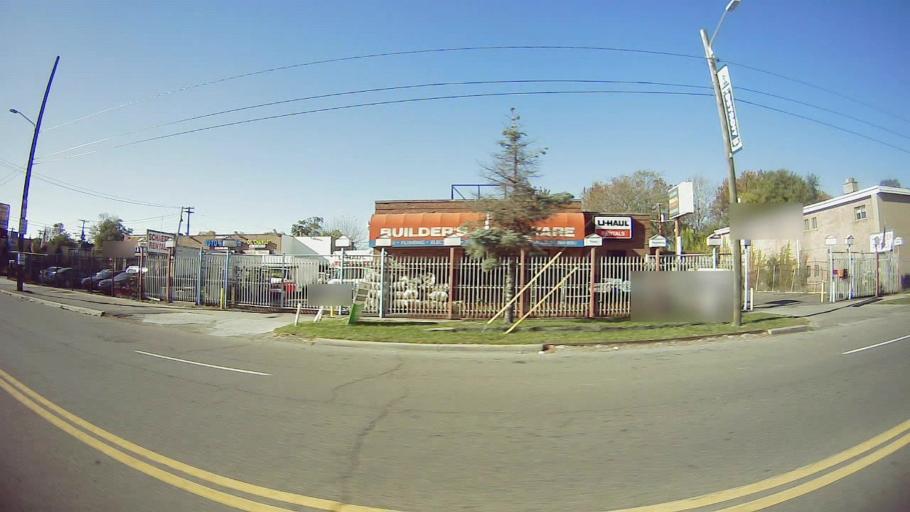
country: US
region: Michigan
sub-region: Wayne County
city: Dearborn
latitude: 42.3518
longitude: -83.1771
